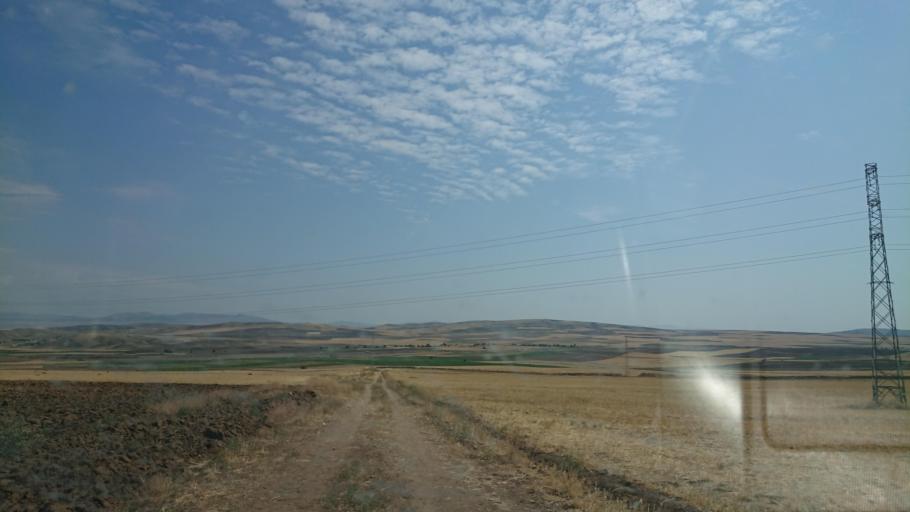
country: TR
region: Aksaray
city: Sariyahsi
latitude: 38.9522
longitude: 33.9101
